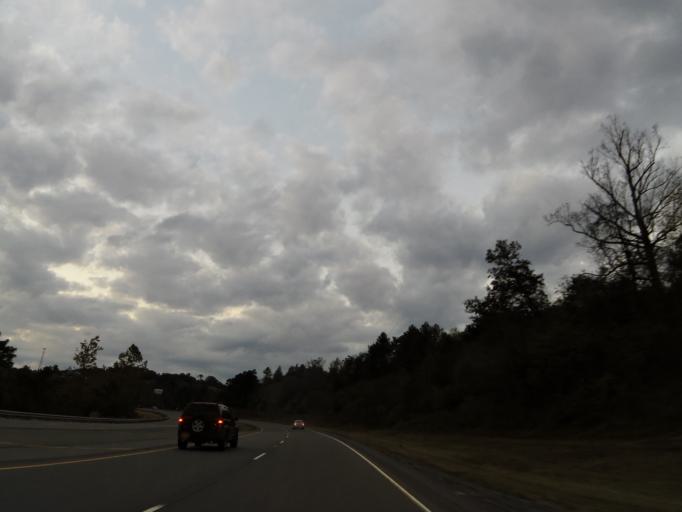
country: US
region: North Carolina
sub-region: Madison County
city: Marshall
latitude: 35.7781
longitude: -82.6318
